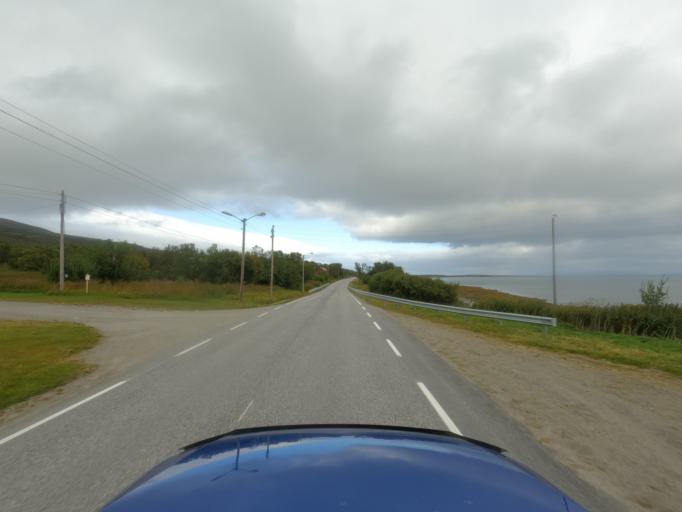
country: NO
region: Finnmark Fylke
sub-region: Porsanger
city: Lakselv
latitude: 70.4467
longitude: 25.2169
